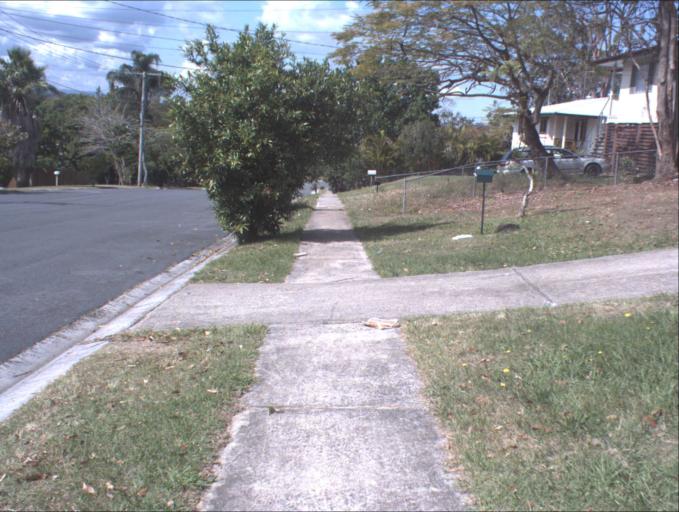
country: AU
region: Queensland
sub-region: Logan
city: Logan City
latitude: -27.6512
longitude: 153.1224
